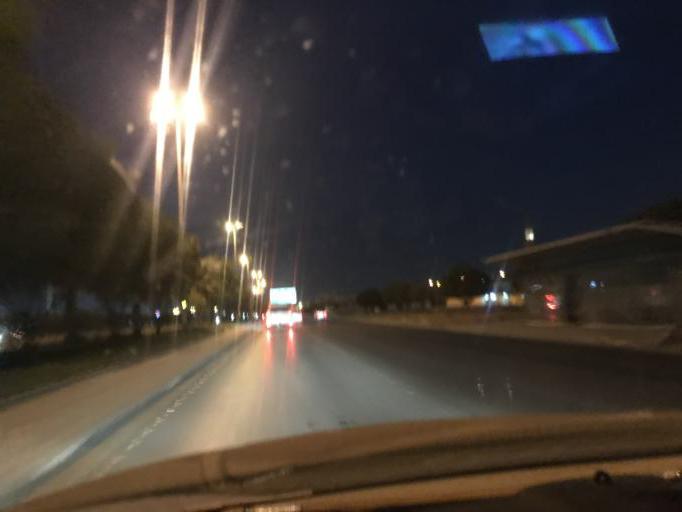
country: SA
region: Ar Riyad
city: Riyadh
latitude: 24.6673
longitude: 46.8008
